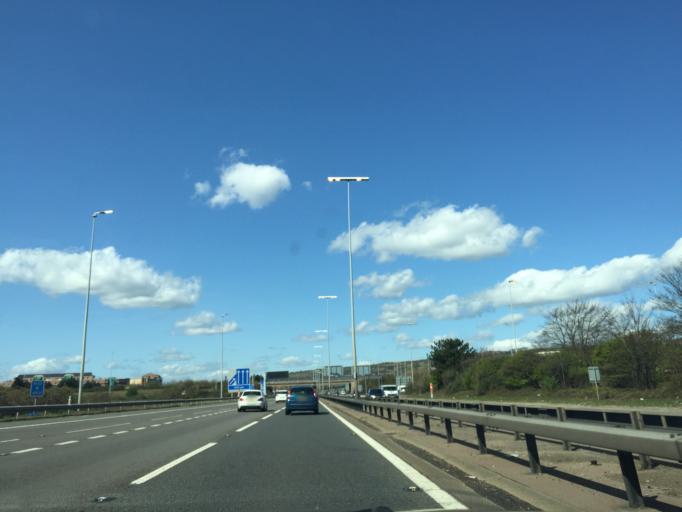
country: GB
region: England
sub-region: Portsmouth
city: Cosham
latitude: 50.8400
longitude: -1.0885
